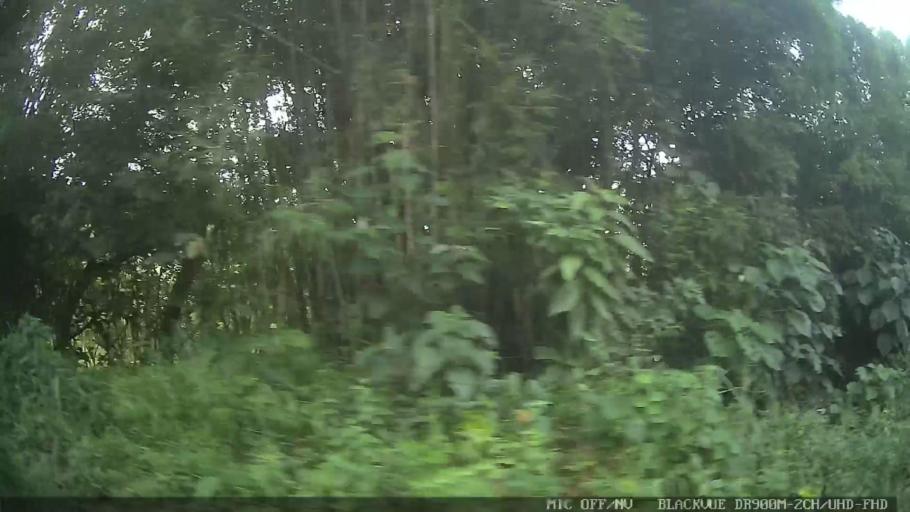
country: BR
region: Minas Gerais
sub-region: Extrema
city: Extrema
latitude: -22.8435
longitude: -46.2918
